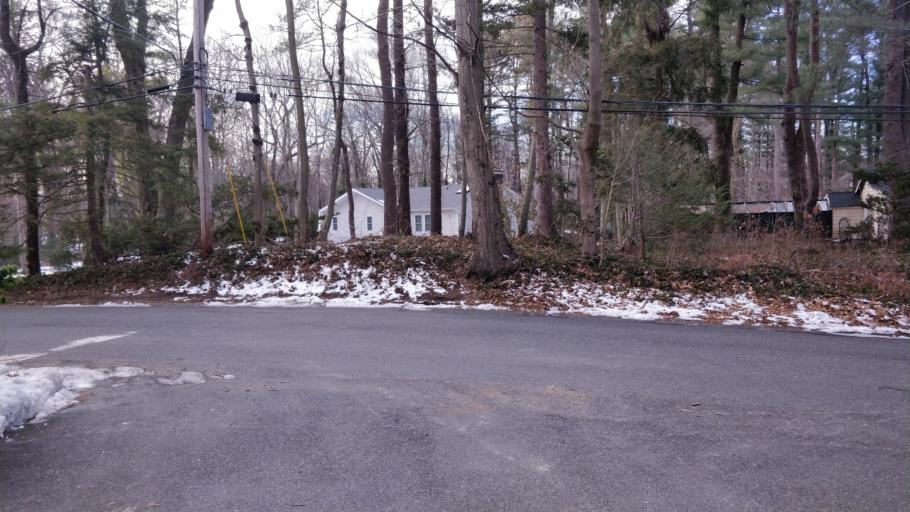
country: US
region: New York
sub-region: Suffolk County
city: Northport
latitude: 40.8846
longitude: -73.3447
